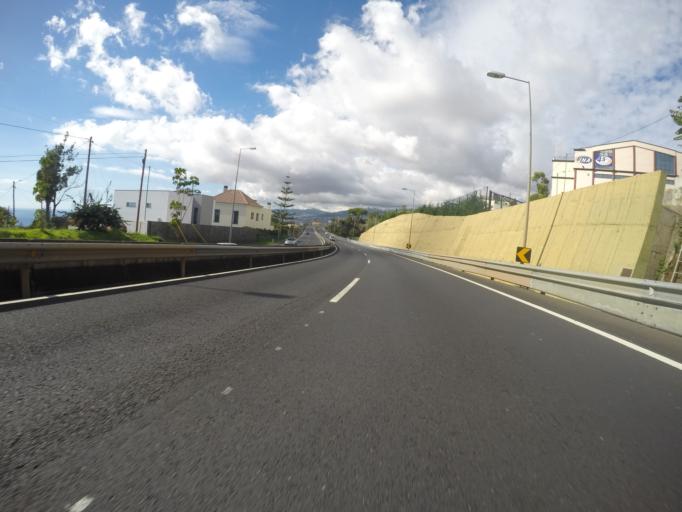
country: PT
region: Madeira
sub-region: Funchal
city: Nossa Senhora do Monte
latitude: 32.6548
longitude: -16.8801
